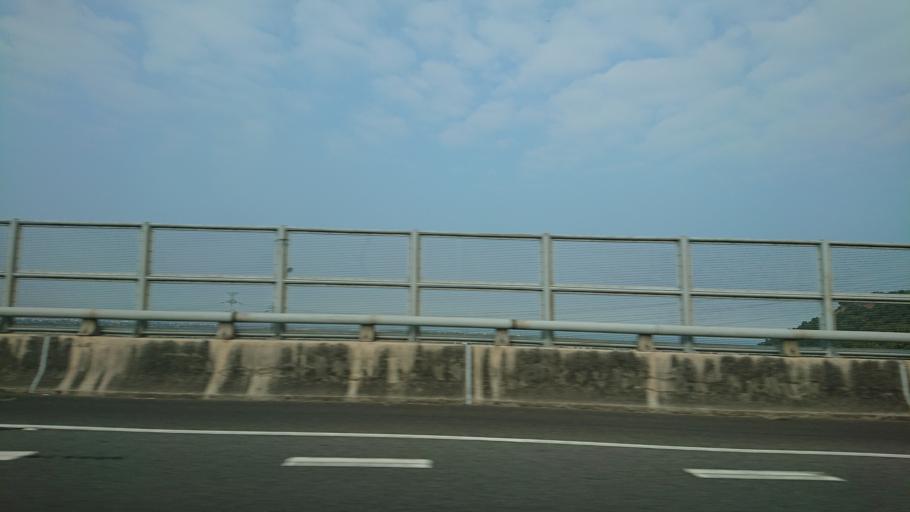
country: TW
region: Taiwan
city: Fengyuan
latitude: 24.3197
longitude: 120.6212
